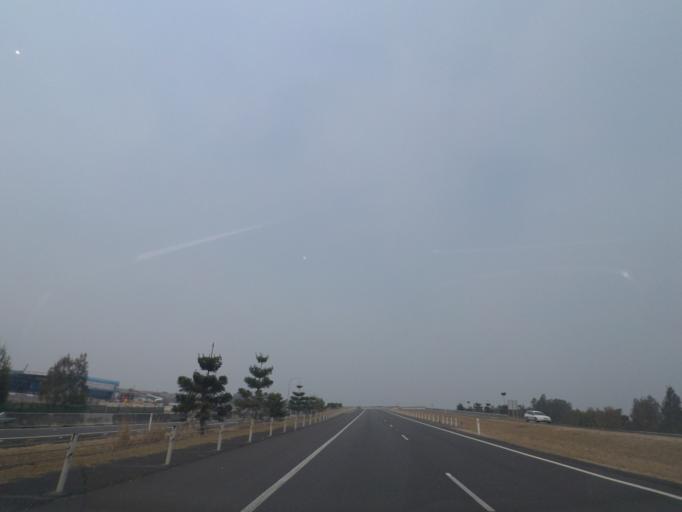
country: AU
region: New South Wales
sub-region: Ballina
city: Ballina
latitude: -28.8624
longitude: 153.5162
